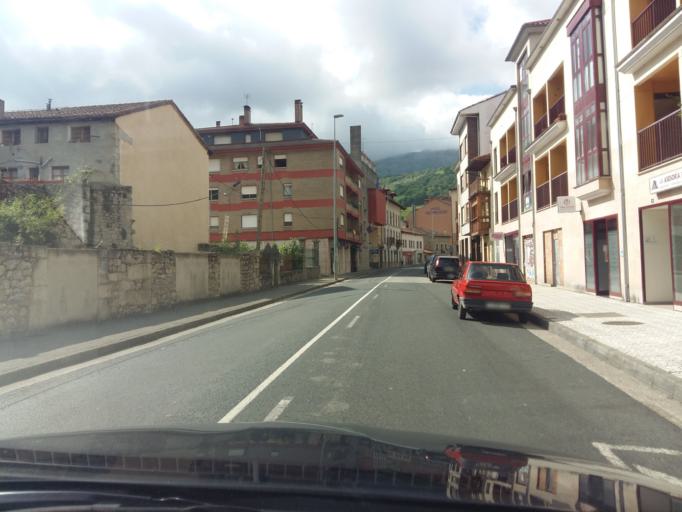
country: ES
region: Cantabria
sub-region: Provincia de Cantabria
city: Tresviso
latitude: 43.3256
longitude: -4.5839
